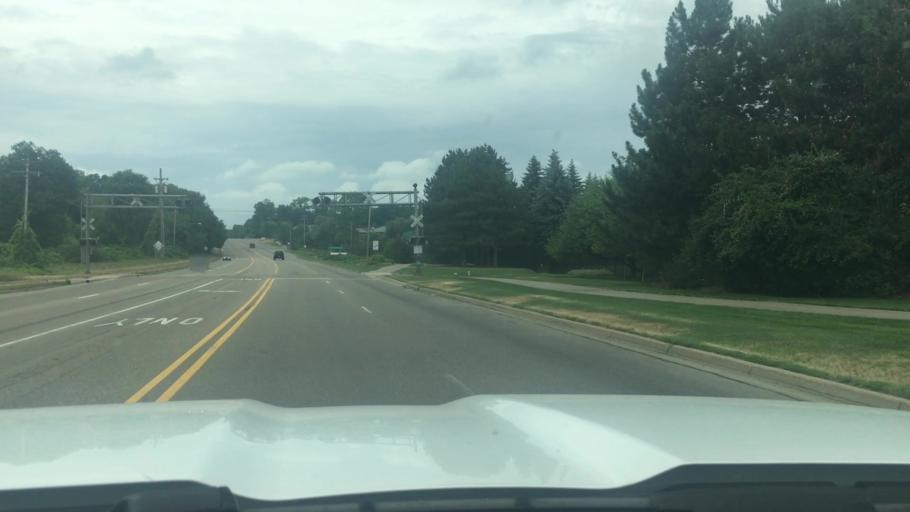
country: US
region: Michigan
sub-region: Kent County
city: Forest Hills
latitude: 42.9597
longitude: -85.4966
